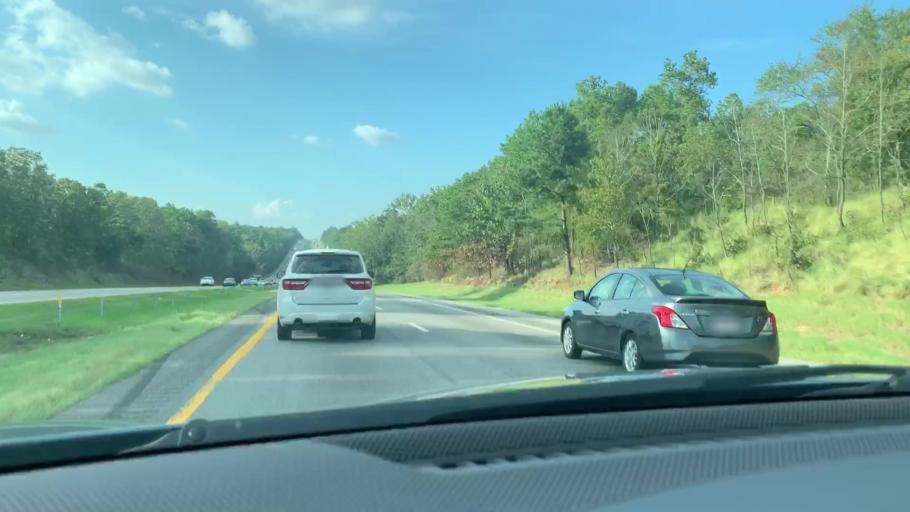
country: US
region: South Carolina
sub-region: Calhoun County
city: Oak Grove
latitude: 33.7185
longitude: -80.9246
